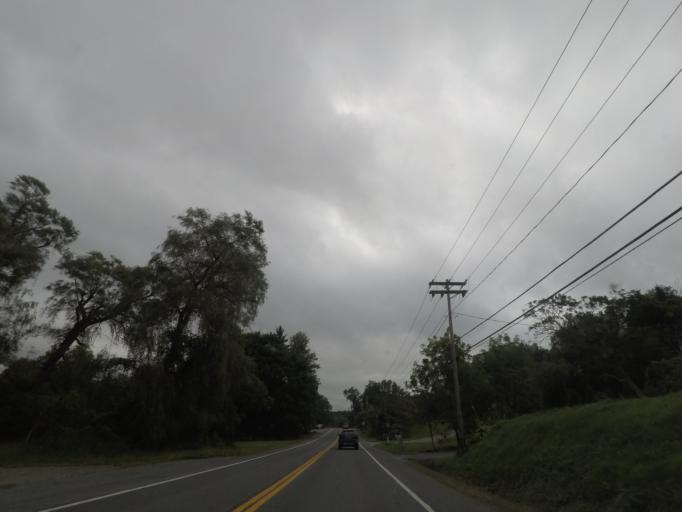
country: US
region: New York
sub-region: Rensselaer County
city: Hoosick Falls
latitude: 42.8887
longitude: -73.3603
